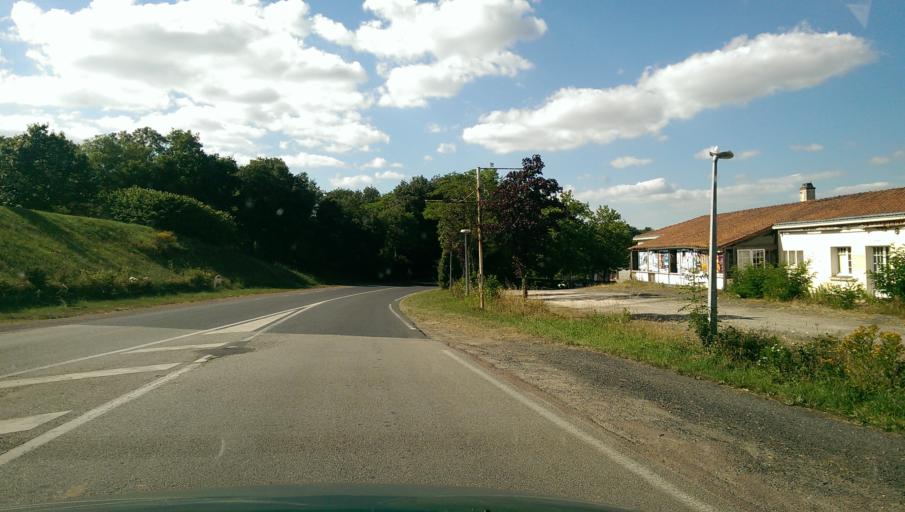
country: FR
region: Pays de la Loire
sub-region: Departement de la Vendee
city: Rocheserviere
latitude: 46.9330
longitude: -1.5140
